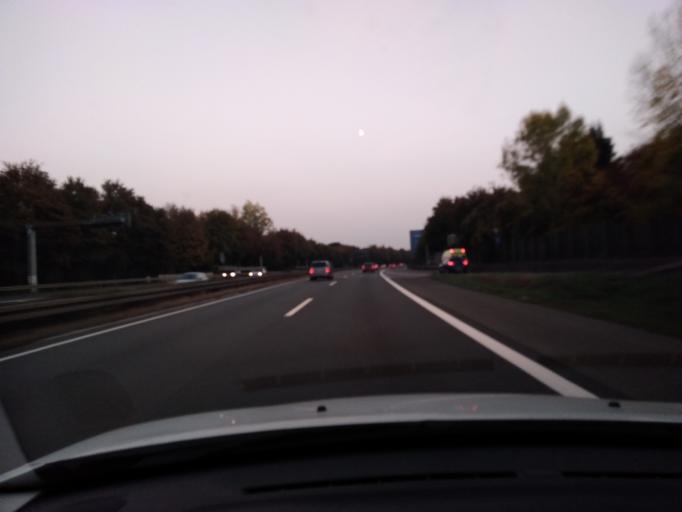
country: DE
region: Saarland
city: Saarbrucken
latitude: 49.2184
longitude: 7.0186
